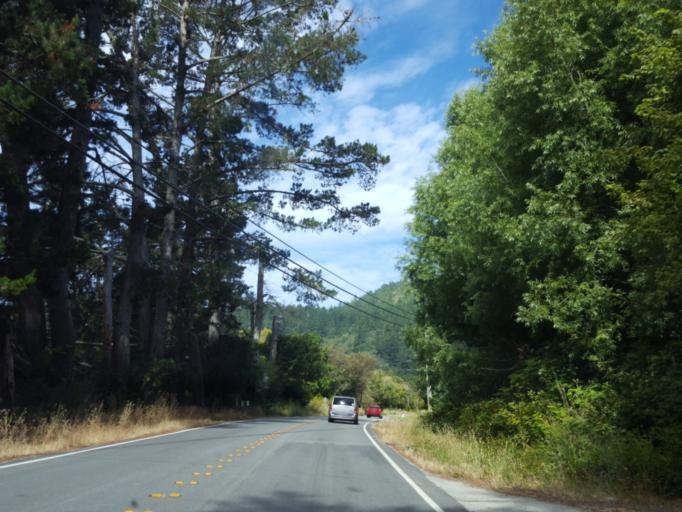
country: US
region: California
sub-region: San Mateo County
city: Portola Valley
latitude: 37.2610
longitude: -122.3306
